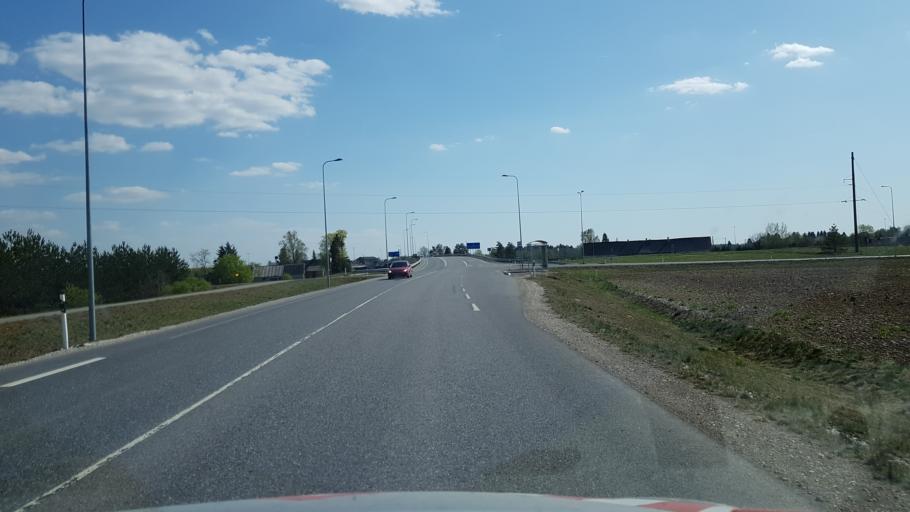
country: EE
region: Harju
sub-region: Raasiku vald
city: Arukula
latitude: 59.1860
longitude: 25.1156
